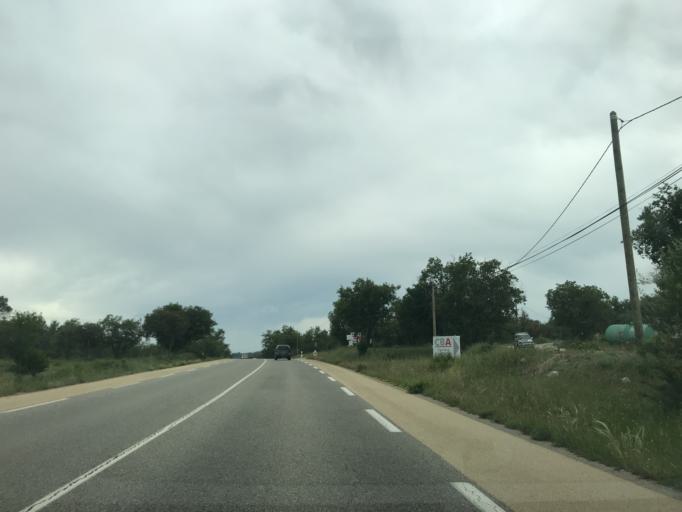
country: FR
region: Provence-Alpes-Cote d'Azur
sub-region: Departement du Var
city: Rians
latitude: 43.5763
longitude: 5.7629
